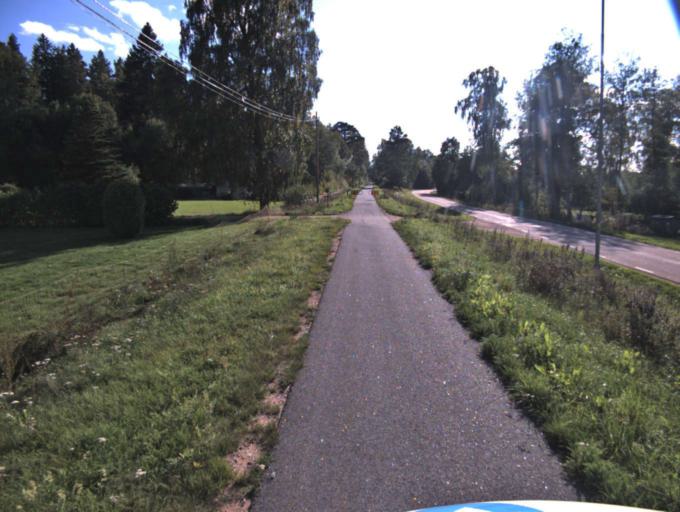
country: SE
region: Vaestra Goetaland
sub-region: Boras Kommun
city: Dalsjofors
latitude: 57.8209
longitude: 13.1538
